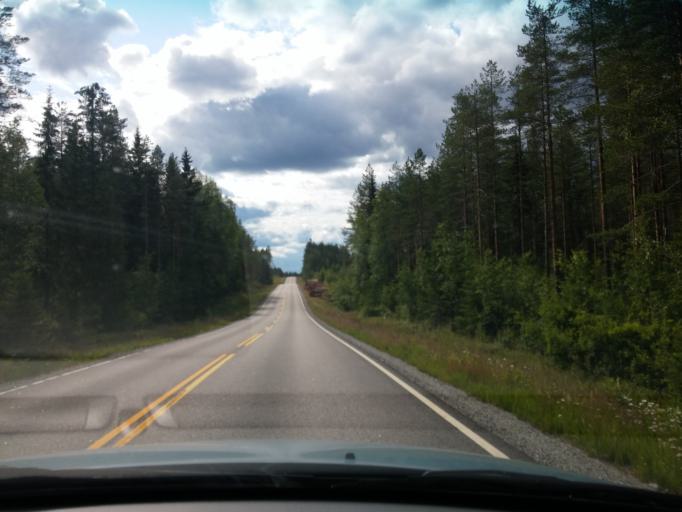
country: FI
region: Central Finland
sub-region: Saarijaervi-Viitasaari
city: Pylkoenmaeki
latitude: 62.6118
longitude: 24.7018
